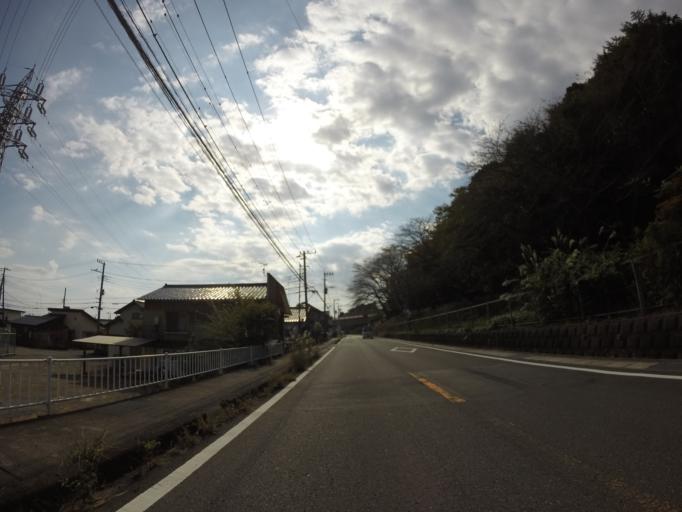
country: JP
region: Shizuoka
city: Fujinomiya
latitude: 35.1790
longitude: 138.6384
